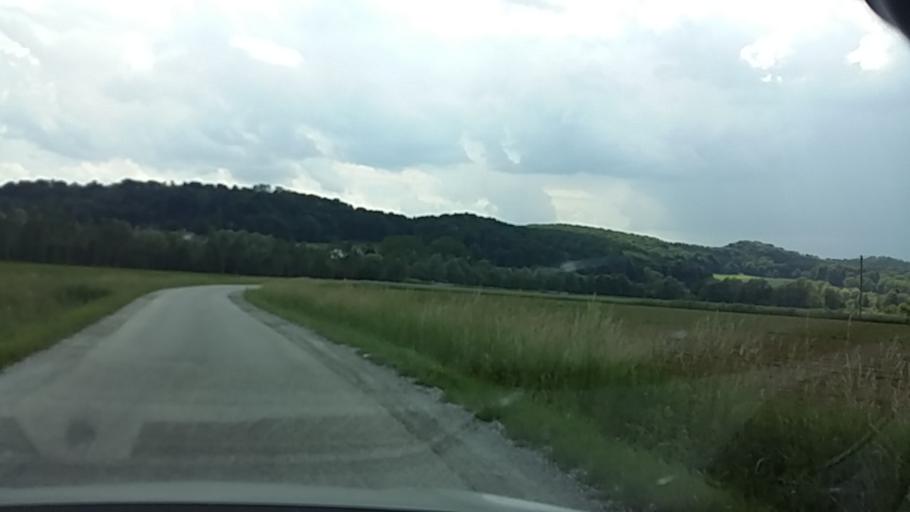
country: AT
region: Styria
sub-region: Politischer Bezirk Hartberg-Fuerstenfeld
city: Soechau
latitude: 47.0652
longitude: 16.0123
